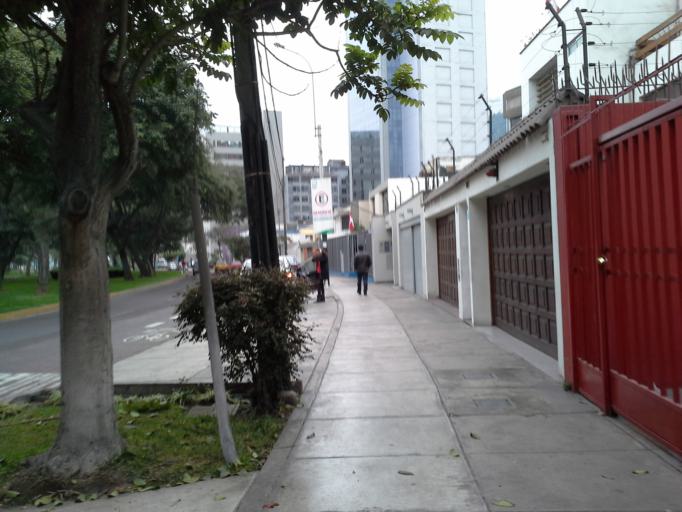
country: PE
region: Lima
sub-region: Lima
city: San Luis
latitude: -12.0986
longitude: -77.0188
